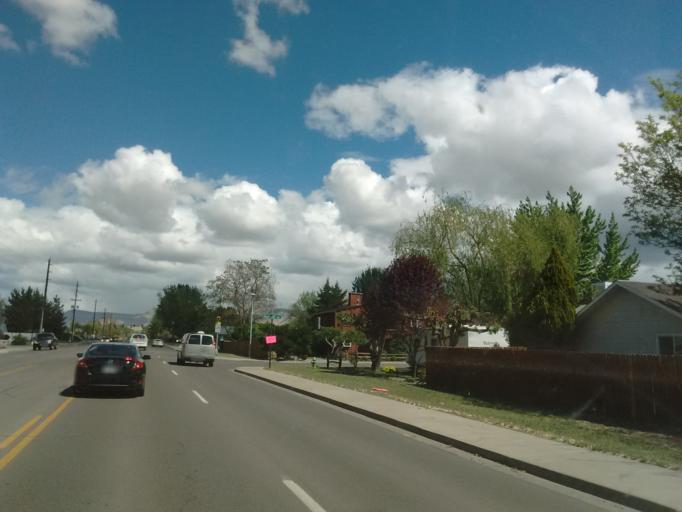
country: US
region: Colorado
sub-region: Mesa County
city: Fruitvale
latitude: 39.0868
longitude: -108.4965
